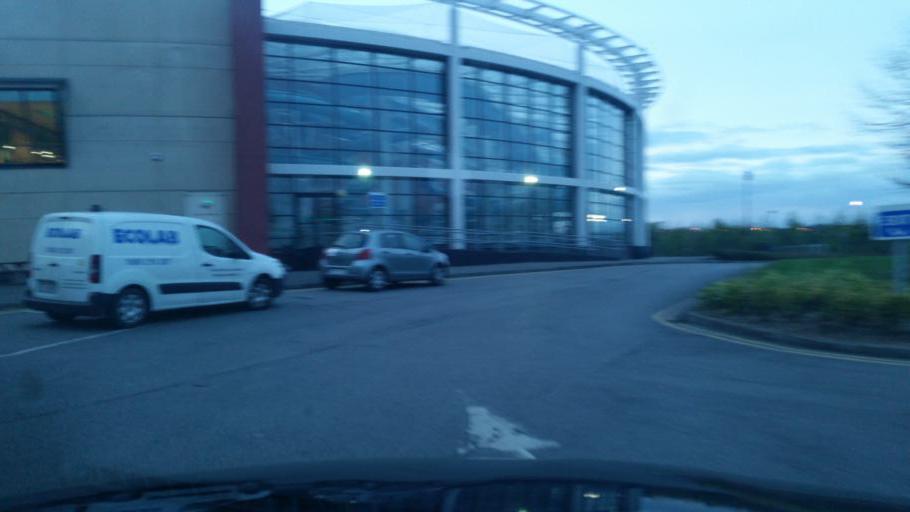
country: IE
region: Leinster
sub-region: Fingal County
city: Blanchardstown
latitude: 53.3965
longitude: -6.3699
